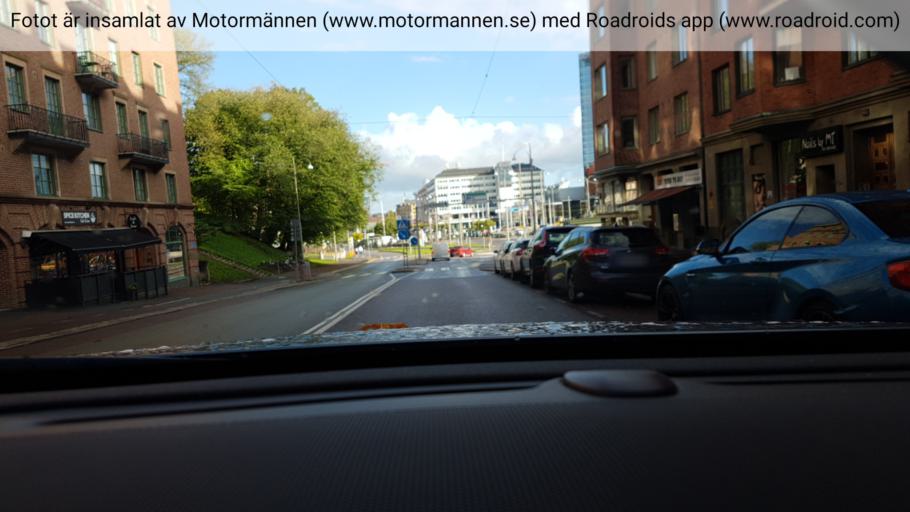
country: SE
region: Vaestra Goetaland
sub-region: Goteborg
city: Goeteborg
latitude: 57.6936
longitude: 11.9870
